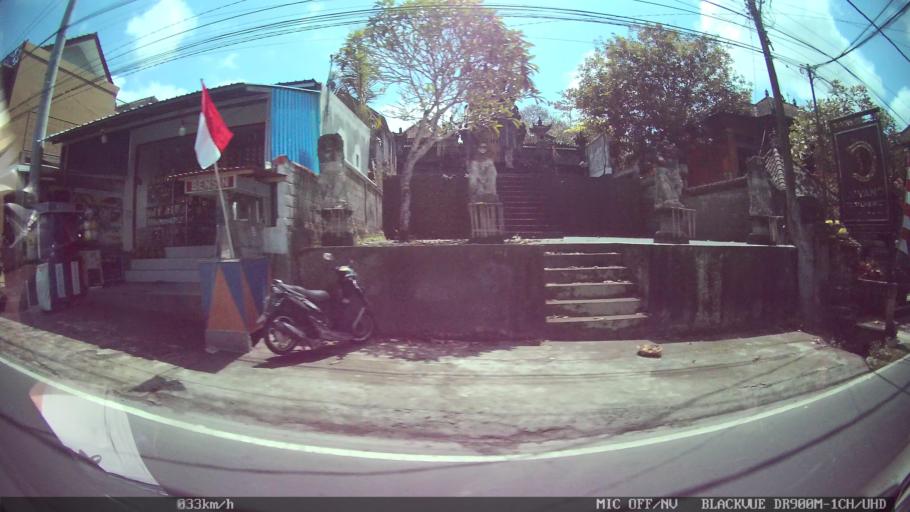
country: ID
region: Bali
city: Banjar Jabejero
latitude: -8.5920
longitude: 115.2652
